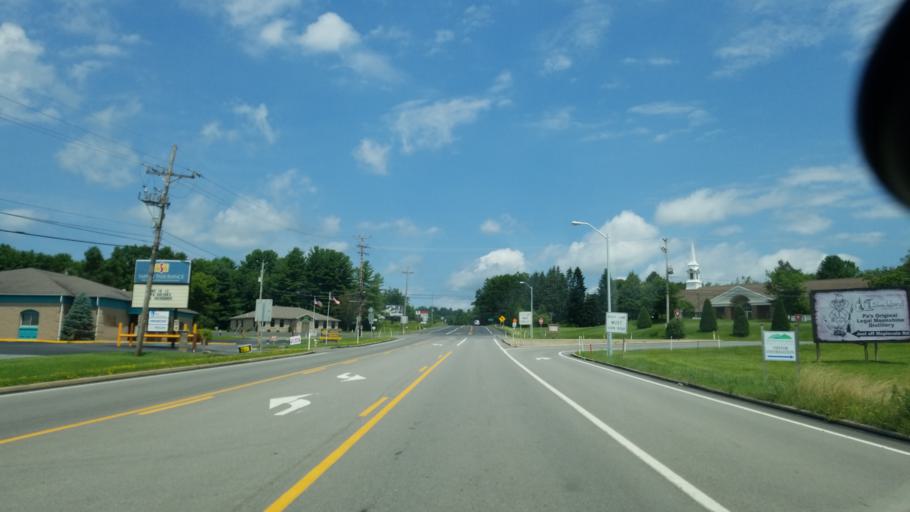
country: US
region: Pennsylvania
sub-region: Jefferson County
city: Brookville
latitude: 41.1762
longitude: -79.0984
